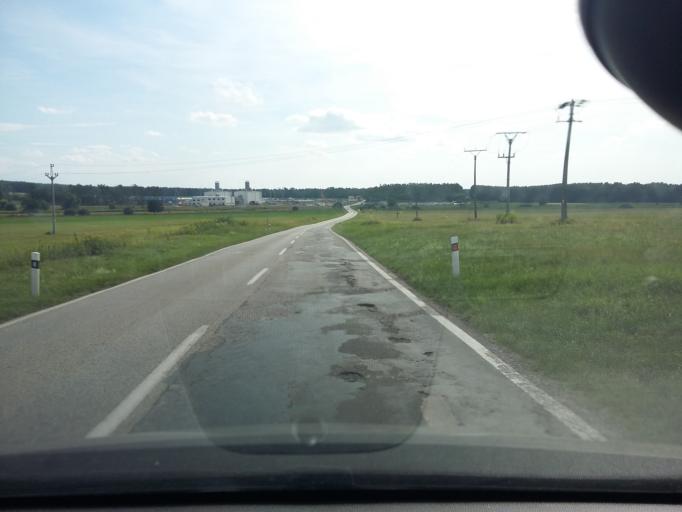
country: SK
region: Trnavsky
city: Gbely
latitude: 48.6022
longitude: 17.1978
